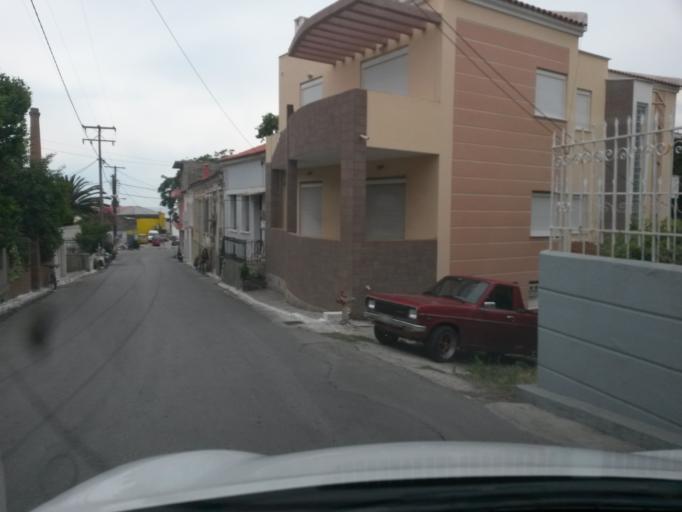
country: GR
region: North Aegean
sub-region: Nomos Lesvou
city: Plomarion
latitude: 38.9743
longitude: 26.3771
